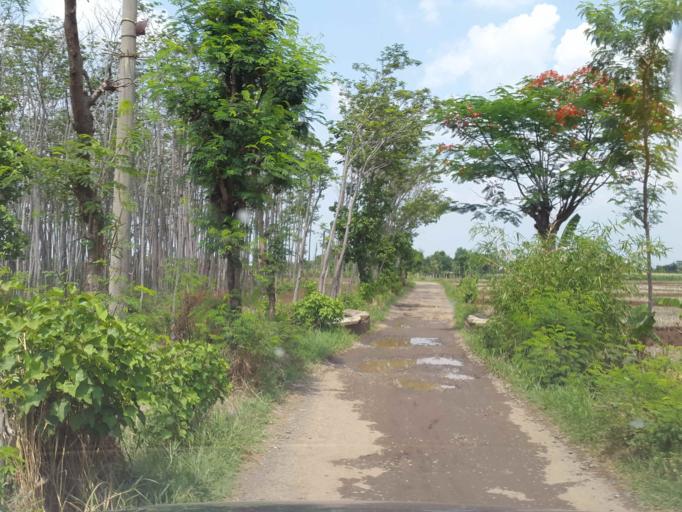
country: ID
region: Central Java
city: Balapulang
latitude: -7.0603
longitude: 109.0399
